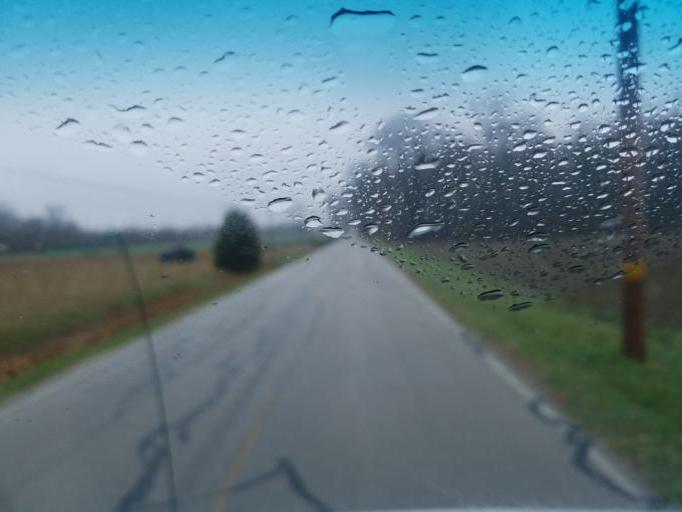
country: US
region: Ohio
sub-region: Wood County
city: North Baltimore
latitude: 41.1956
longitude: -83.6310
